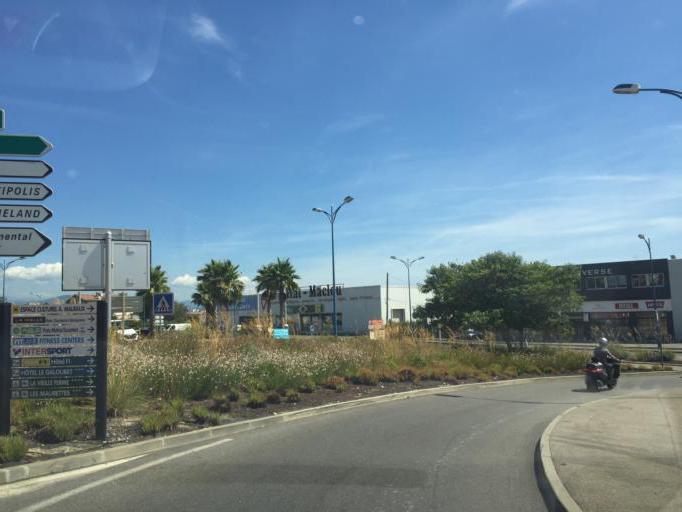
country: FR
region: Provence-Alpes-Cote d'Azur
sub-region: Departement des Alpes-Maritimes
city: Villeneuve-Loubet
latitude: 43.6375
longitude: 7.1328
